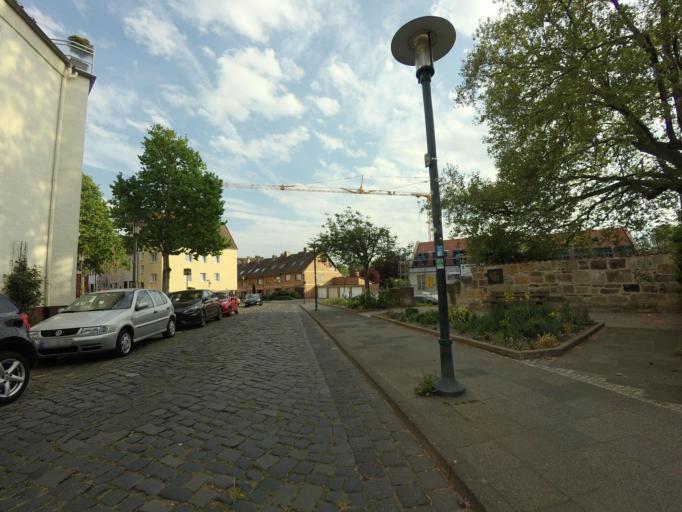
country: DE
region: Lower Saxony
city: Hildesheim
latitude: 52.1508
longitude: 9.9420
